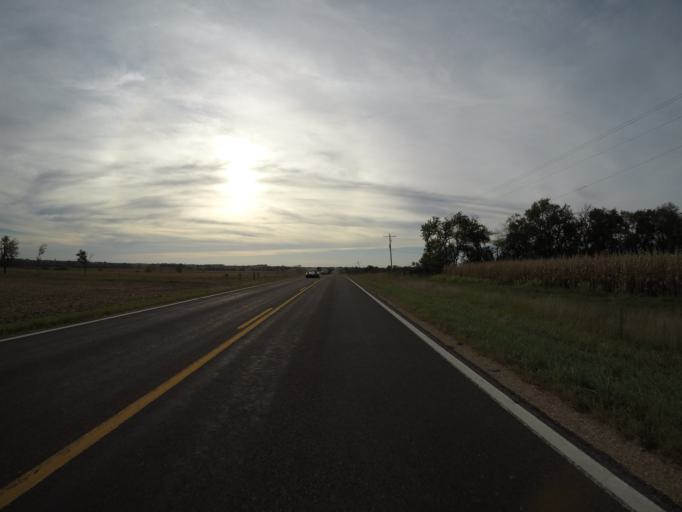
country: US
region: Kansas
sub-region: Osage County
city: Overbrook
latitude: 38.7825
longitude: -95.3804
